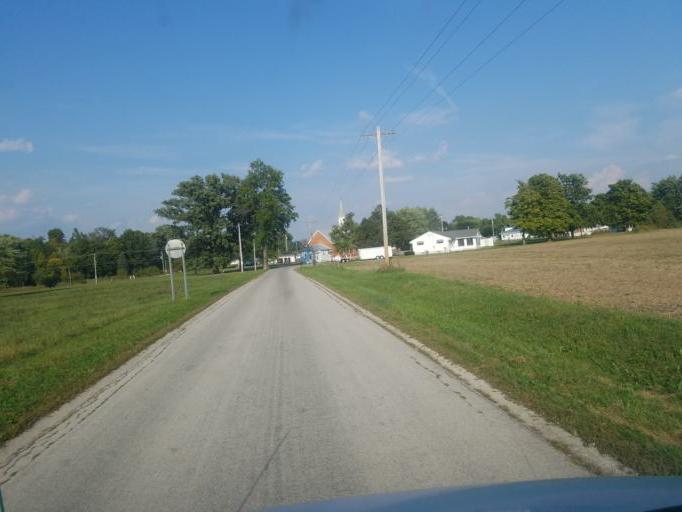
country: US
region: Ohio
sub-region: Wyandot County
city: Carey
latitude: 40.9193
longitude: -83.3488
